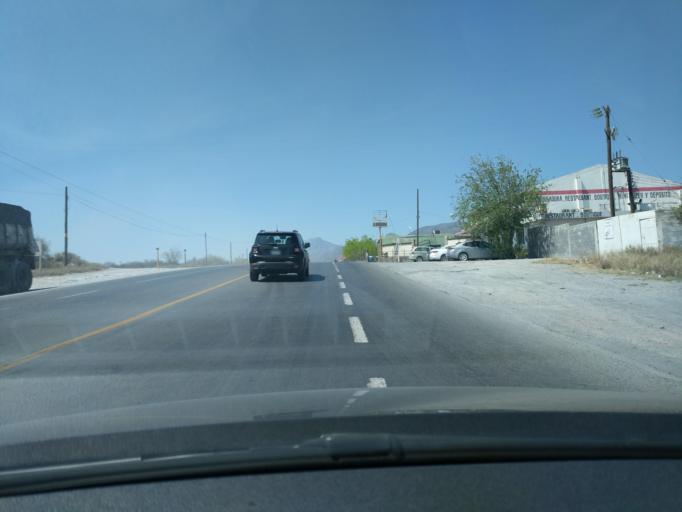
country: MX
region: Nuevo Leon
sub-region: Salinas Victoria
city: Las Torres
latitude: 25.9206
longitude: -100.3690
